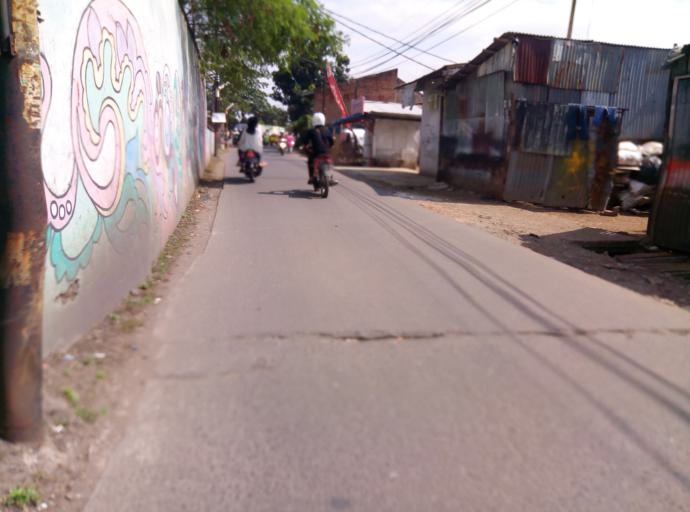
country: ID
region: West Java
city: Bandung
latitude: -6.9301
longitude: 107.6504
